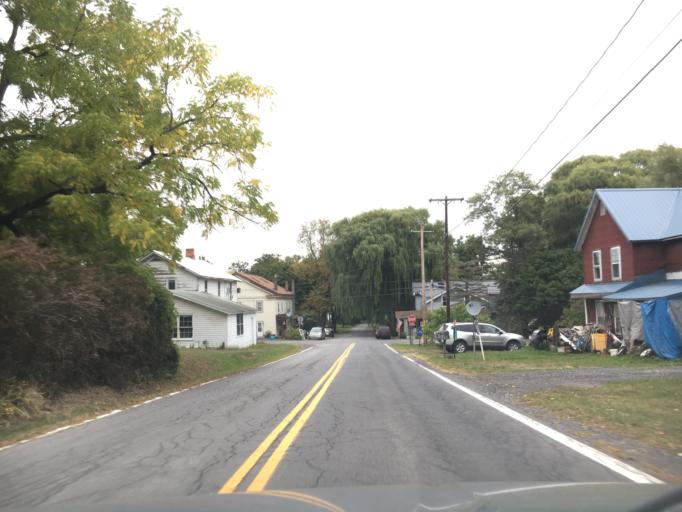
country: US
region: New York
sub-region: Tompkins County
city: Trumansburg
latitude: 42.6647
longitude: -76.7023
